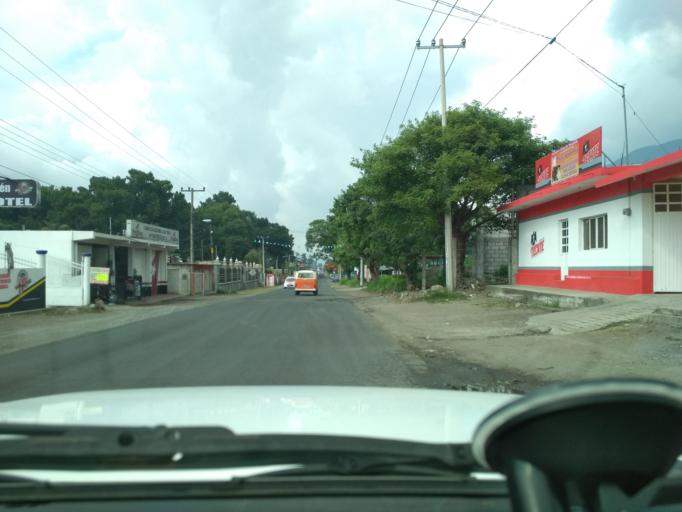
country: MX
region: Veracruz
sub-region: Nogales
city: Taza de Agua Ojo Zarco
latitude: 18.7874
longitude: -97.1991
